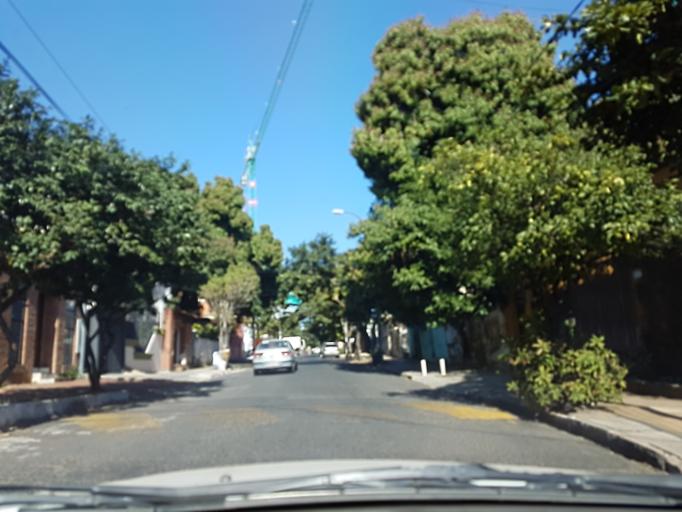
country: PY
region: Asuncion
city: Asuncion
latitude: -25.2822
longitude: -57.6032
